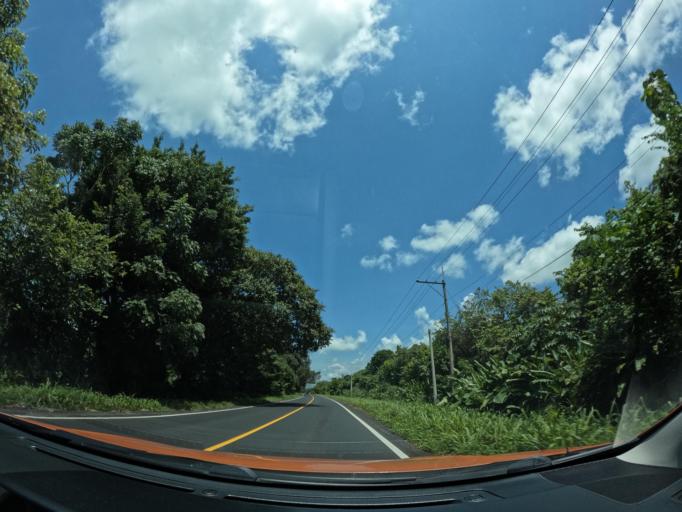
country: GT
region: Escuintla
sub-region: Municipio de Masagua
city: Masagua
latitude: 14.1746
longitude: -90.8712
